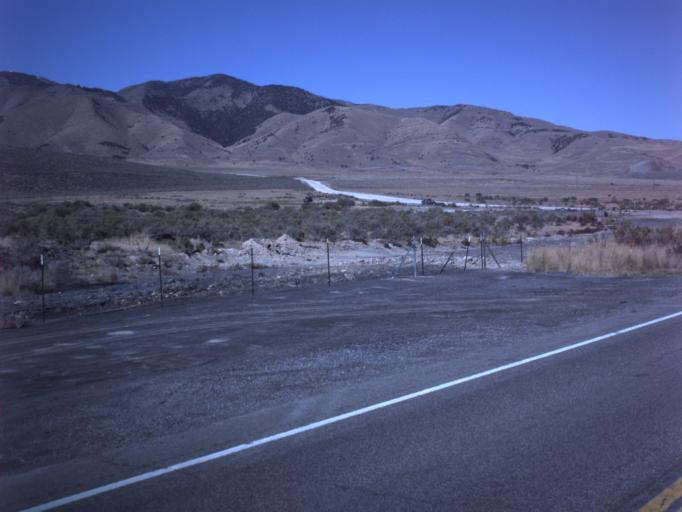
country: US
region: Utah
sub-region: Tooele County
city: Grantsville
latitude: 40.6393
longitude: -112.5227
